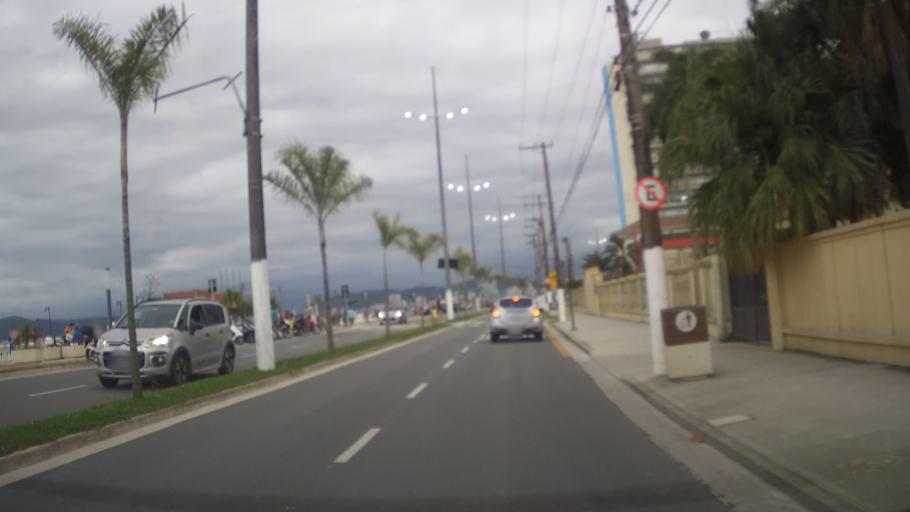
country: BR
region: Sao Paulo
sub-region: Santos
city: Santos
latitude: -23.9907
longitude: -46.3061
